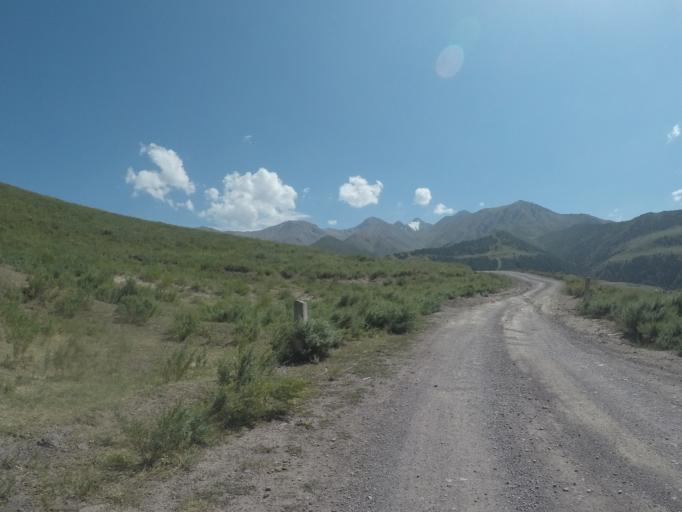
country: KG
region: Chuy
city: Bishkek
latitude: 42.6483
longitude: 74.5214
